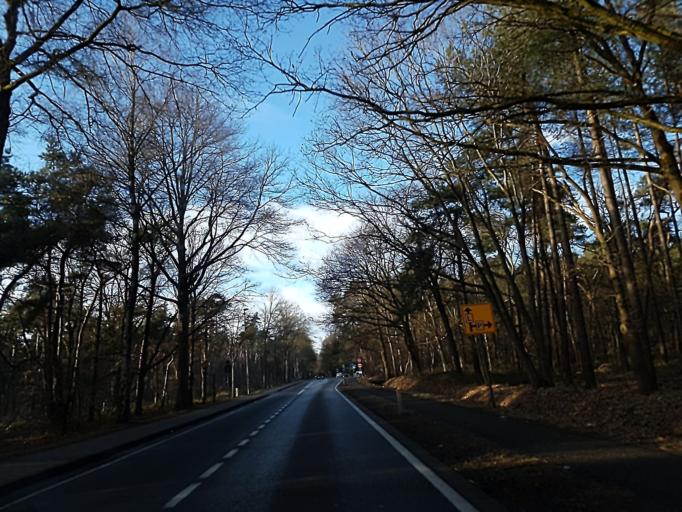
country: BE
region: Flanders
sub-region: Provincie Antwerpen
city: Oud-Turnhout
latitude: 51.3027
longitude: 5.0189
